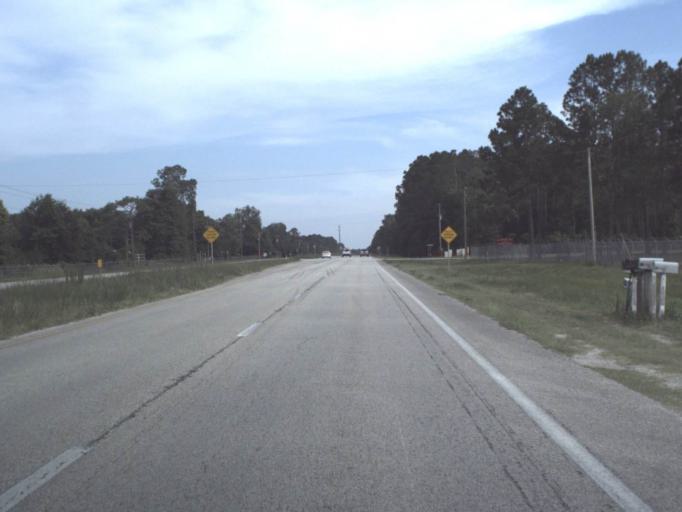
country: US
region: Florida
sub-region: Clay County
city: Green Cove Springs
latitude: 29.9079
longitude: -81.6771
